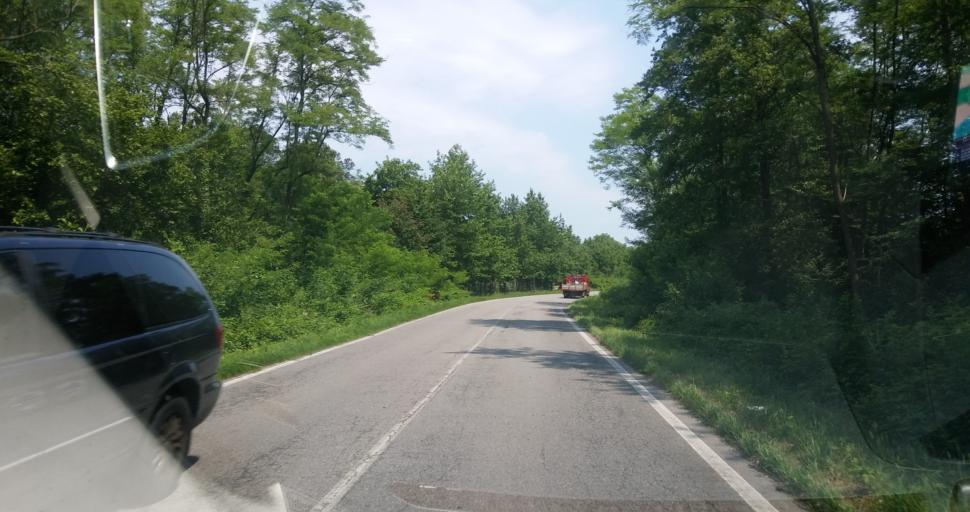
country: IT
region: Lombardy
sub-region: Provincia di Varese
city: Sesto Calende
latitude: 45.7503
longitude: 8.6399
